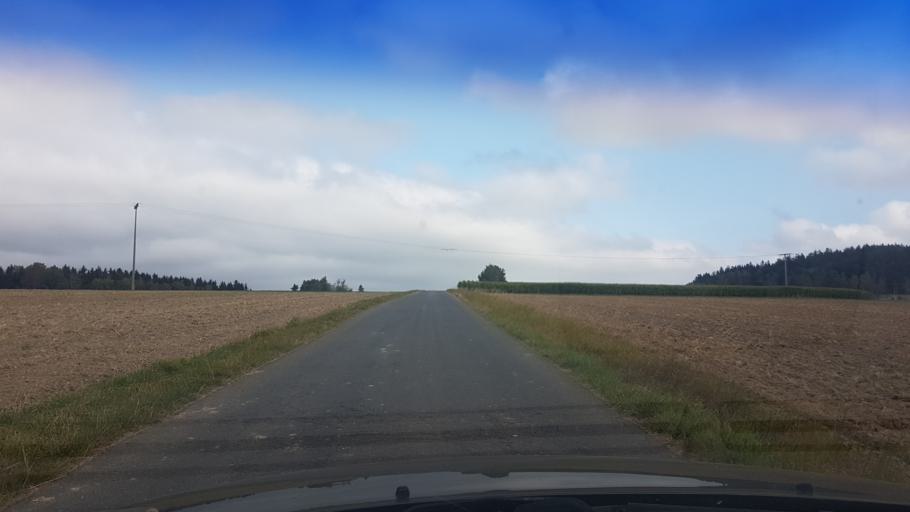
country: DE
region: Bavaria
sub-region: Upper Franconia
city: Wunsiedel
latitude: 50.0774
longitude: 12.0296
